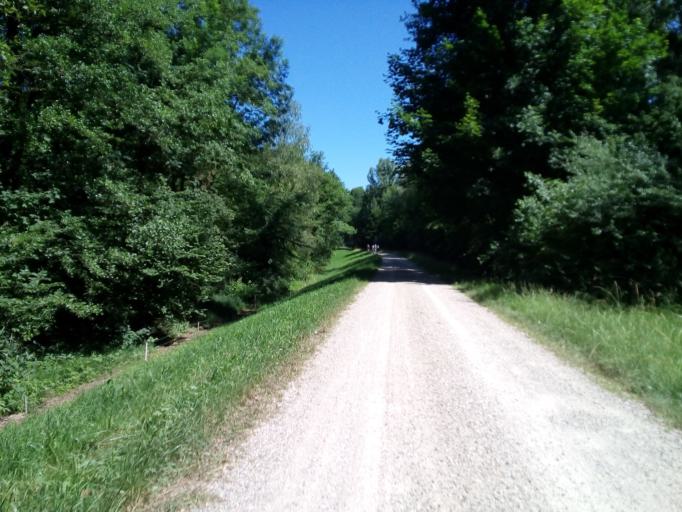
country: DE
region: Baden-Wuerttemberg
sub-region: Freiburg Region
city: Rheinau
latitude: 48.6912
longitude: 7.9507
